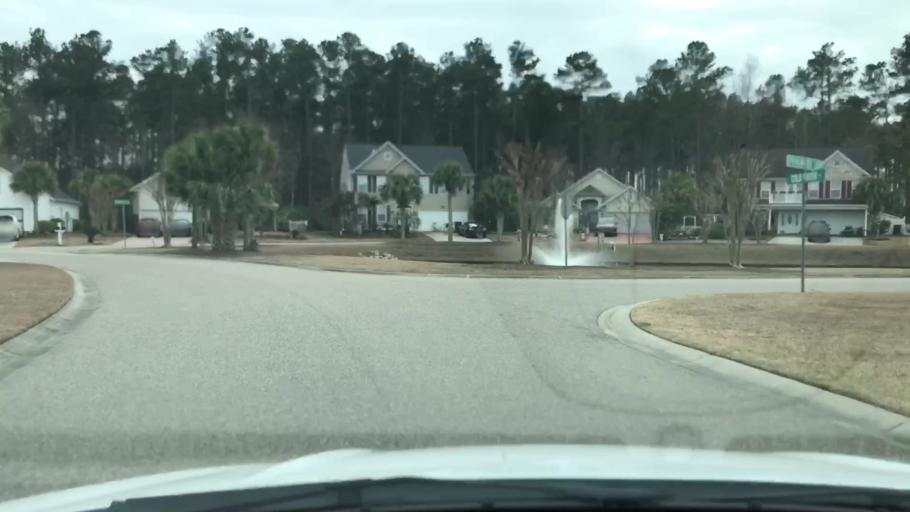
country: US
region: South Carolina
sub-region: Horry County
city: Socastee
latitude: 33.6699
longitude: -78.9741
